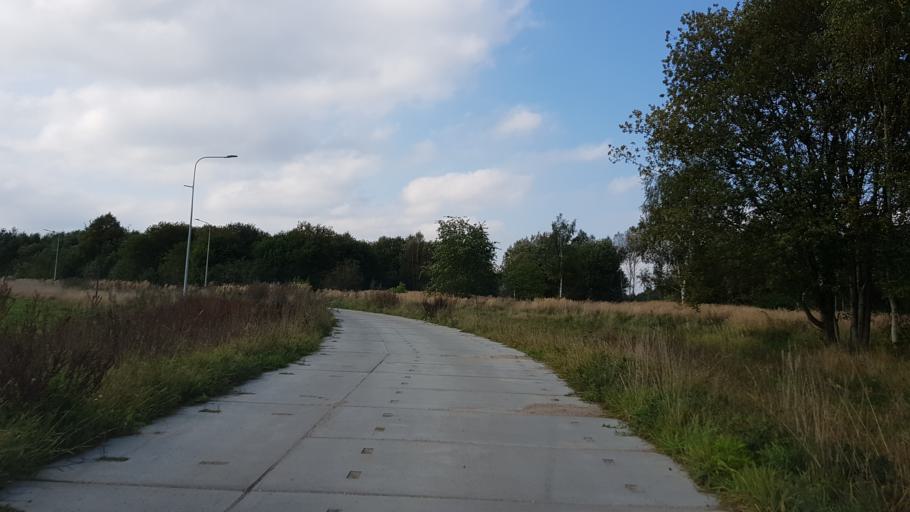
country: PL
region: West Pomeranian Voivodeship
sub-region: Koszalin
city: Koszalin
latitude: 54.1796
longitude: 16.1624
